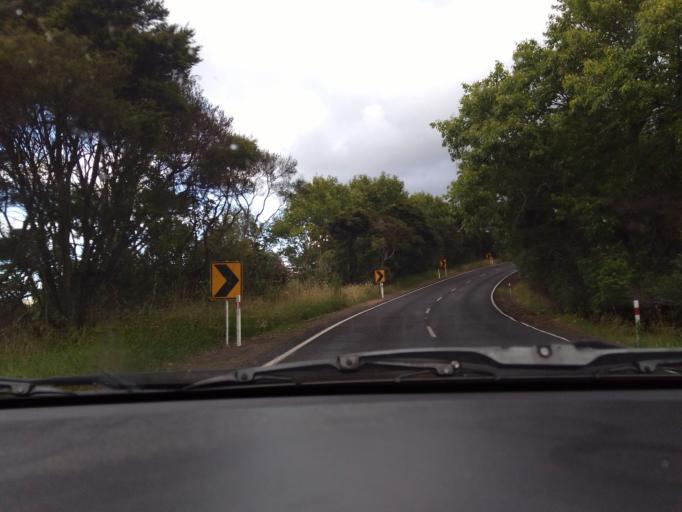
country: NZ
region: Auckland
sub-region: Auckland
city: Titirangi
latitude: -37.0069
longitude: 174.5812
